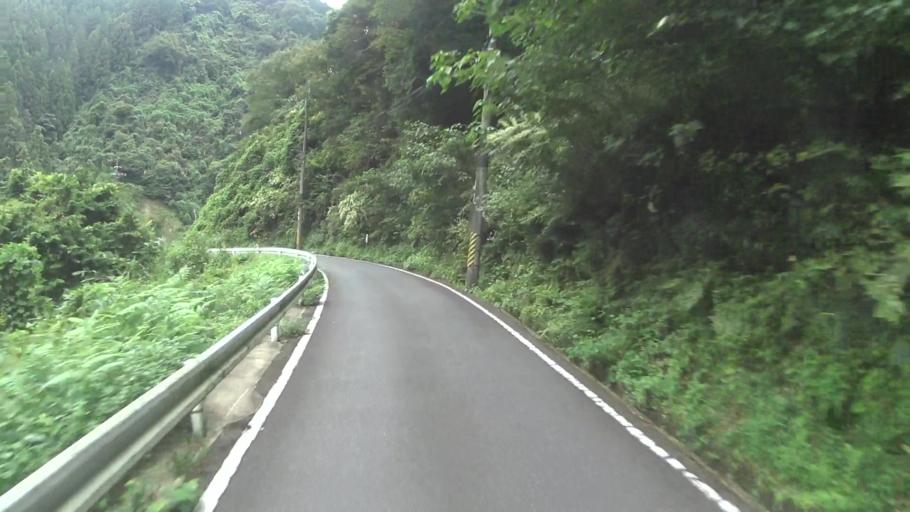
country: JP
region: Kyoto
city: Tanabe
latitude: 34.8040
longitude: 135.8392
